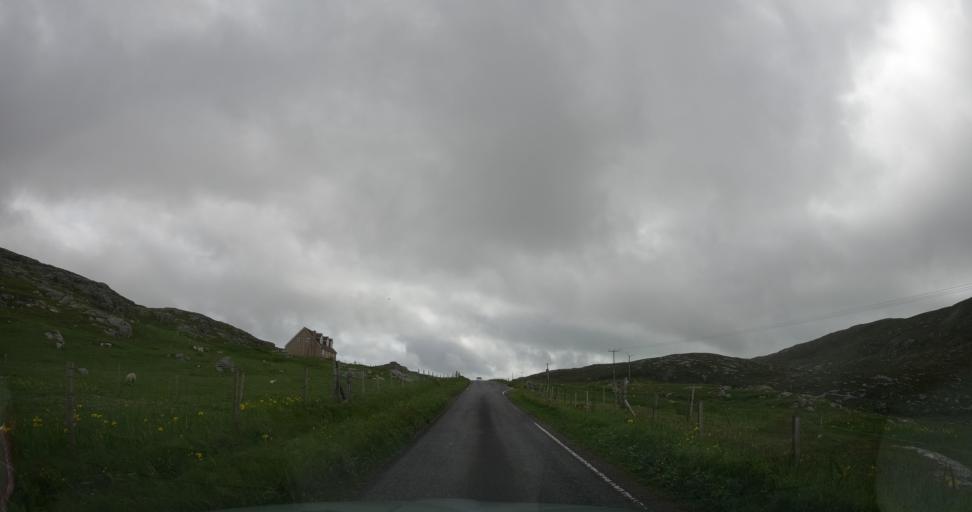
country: GB
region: Scotland
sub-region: Eilean Siar
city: Barra
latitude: 56.9674
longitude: -7.5144
